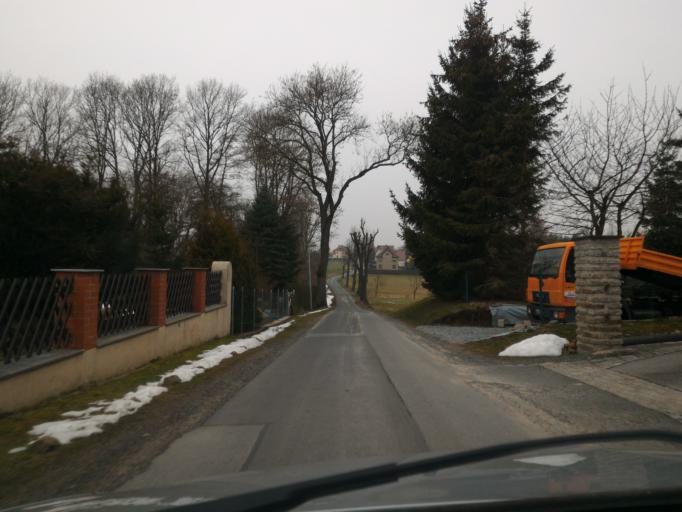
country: DE
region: Saxony
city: Neugersdorf
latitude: 50.9729
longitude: 14.6243
